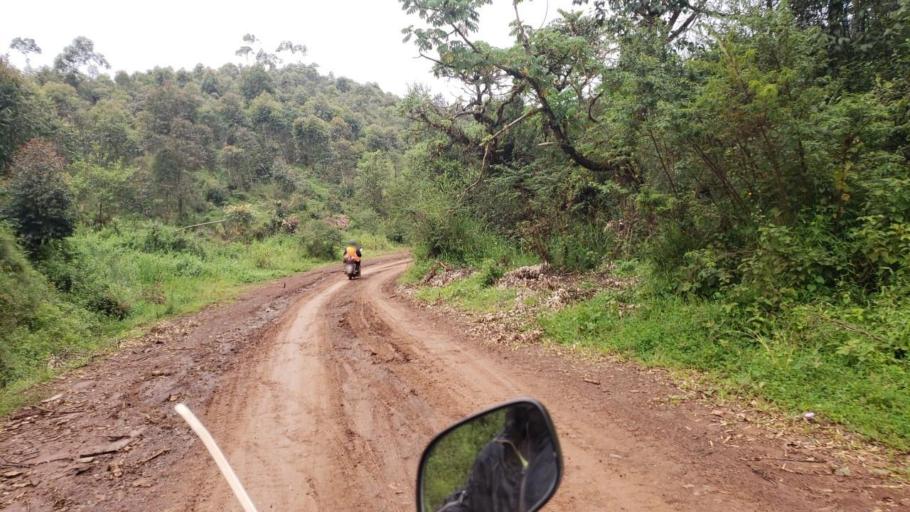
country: CD
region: South Kivu
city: Kabare
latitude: -2.2690
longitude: 28.6625
